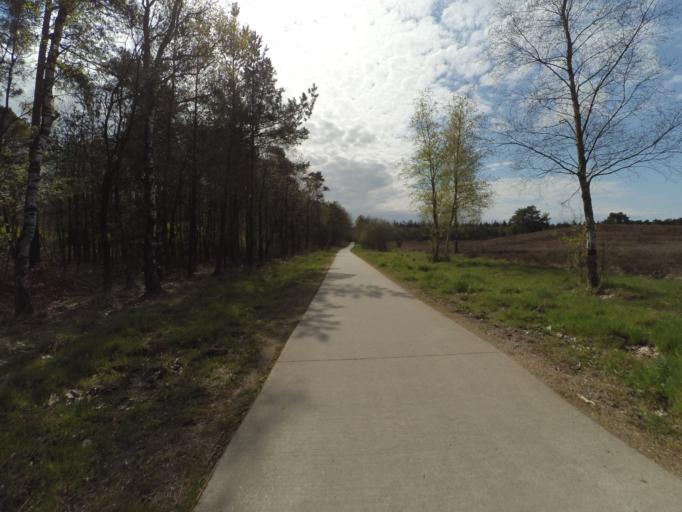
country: NL
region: Gelderland
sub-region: Gemeente Oldebroek
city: Oldebroek
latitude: 52.3818
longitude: 5.9198
